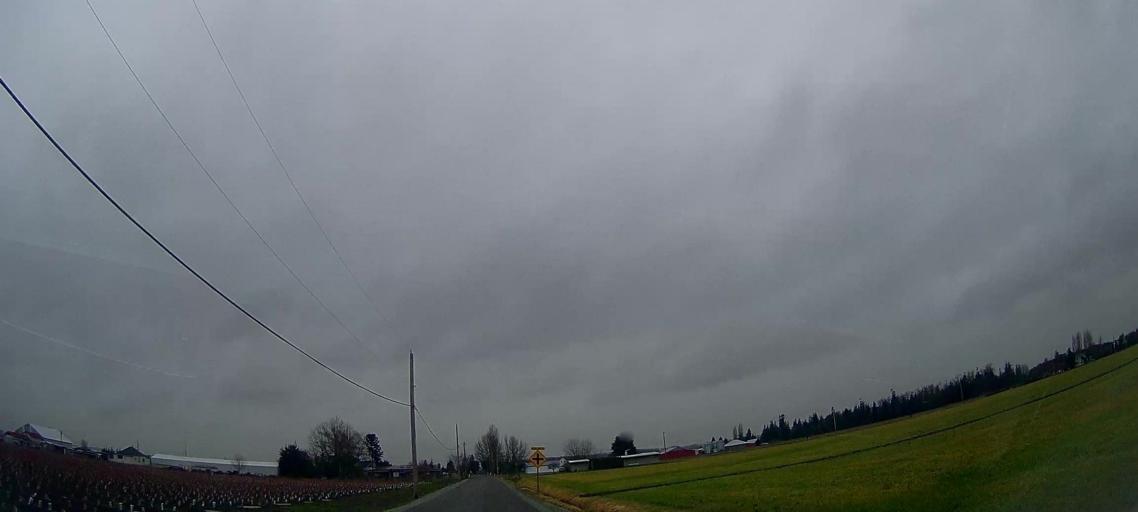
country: US
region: Washington
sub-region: Skagit County
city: Mount Vernon
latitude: 48.3704
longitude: -122.3211
